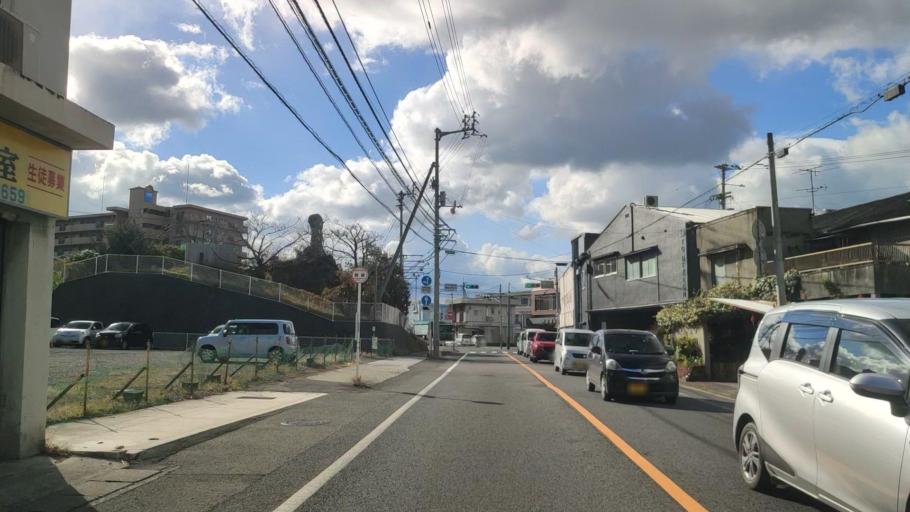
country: JP
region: Ehime
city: Masaki-cho
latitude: 33.8306
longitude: 132.7087
